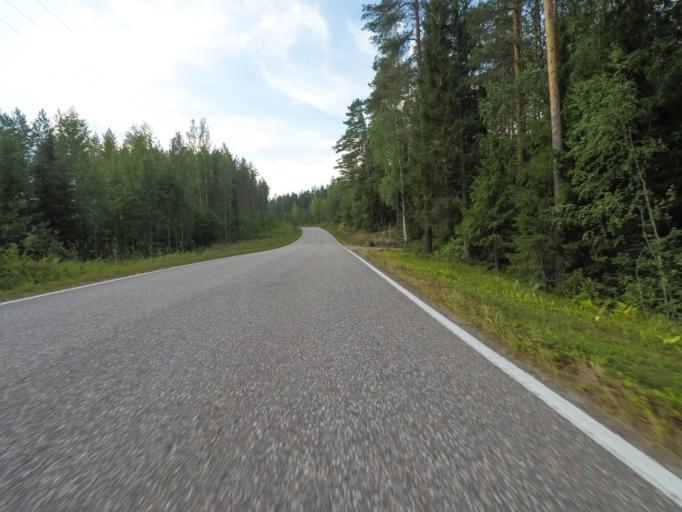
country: FI
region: Southern Savonia
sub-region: Savonlinna
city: Sulkava
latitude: 61.7350
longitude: 28.2071
